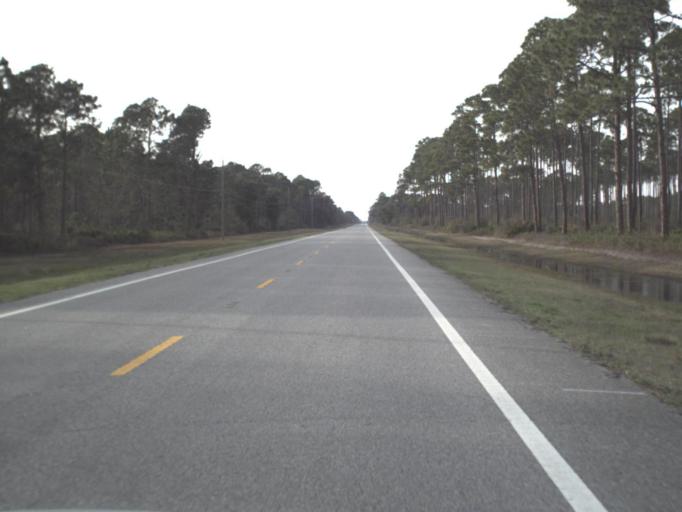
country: US
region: Florida
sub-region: Bay County
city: Tyndall Air Force Base
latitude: 30.0364
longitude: -85.5466
